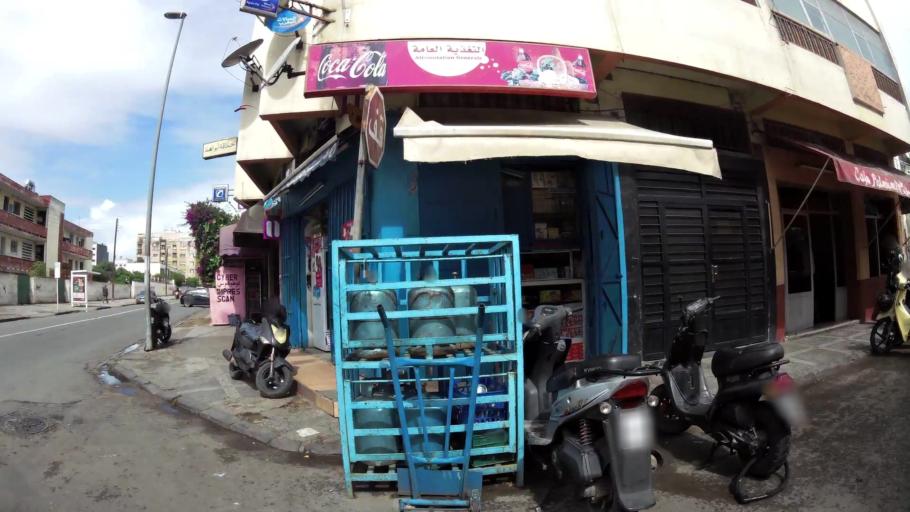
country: MA
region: Grand Casablanca
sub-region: Casablanca
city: Casablanca
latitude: 33.5782
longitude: -7.6303
